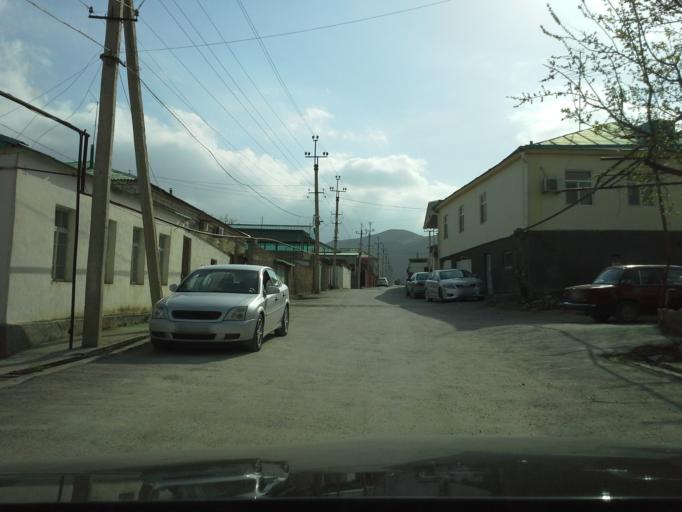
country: TM
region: Ahal
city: Abadan
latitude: 37.9565
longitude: 58.2102
